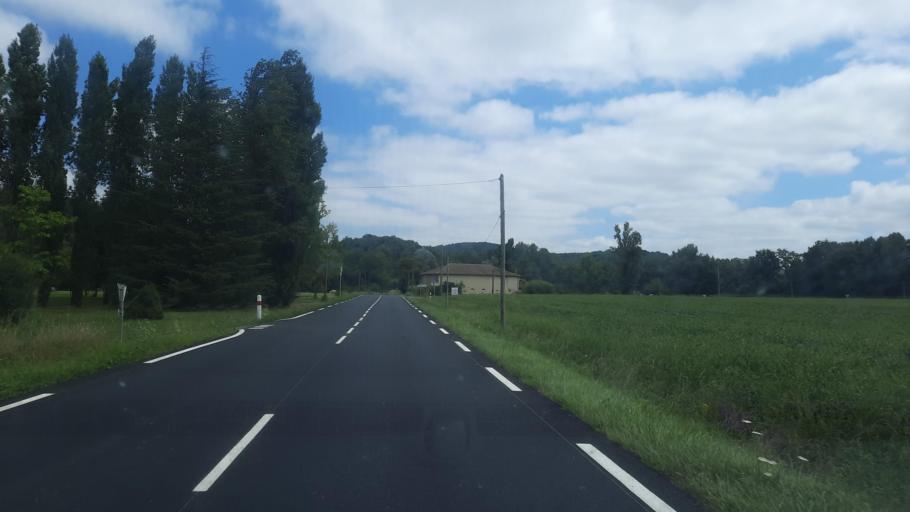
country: FR
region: Midi-Pyrenees
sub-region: Departement de la Haute-Garonne
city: Boulogne-sur-Gesse
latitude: 43.2872
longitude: 0.5400
